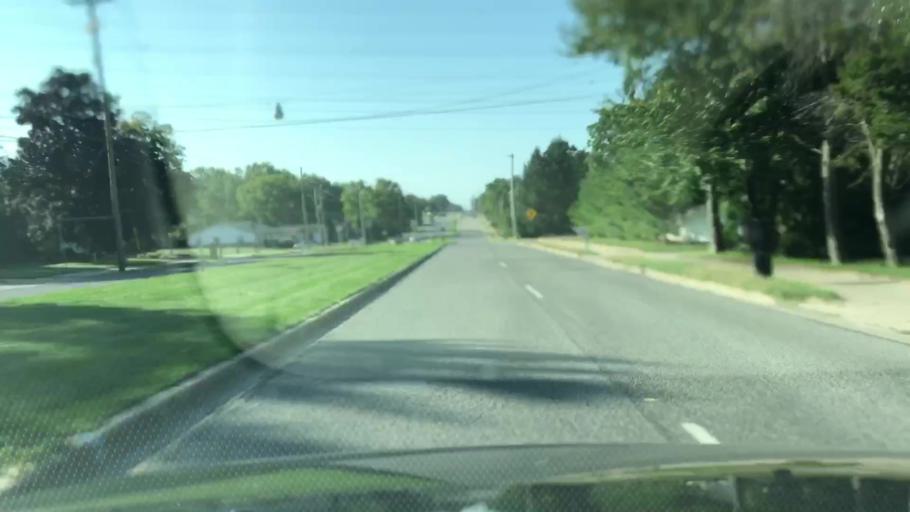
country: US
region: Michigan
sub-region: Kent County
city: Kentwood
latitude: 42.8736
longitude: -85.6256
